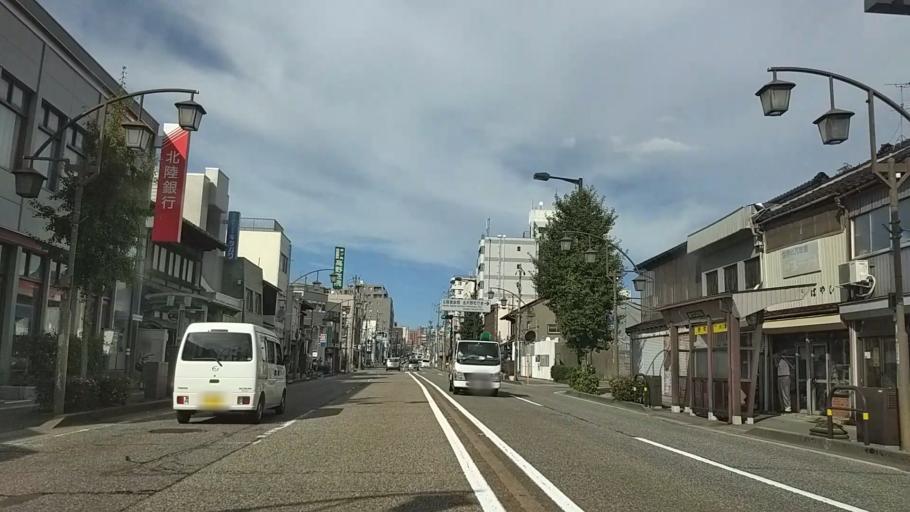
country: JP
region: Ishikawa
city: Nonoichi
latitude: 36.5528
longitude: 136.6461
